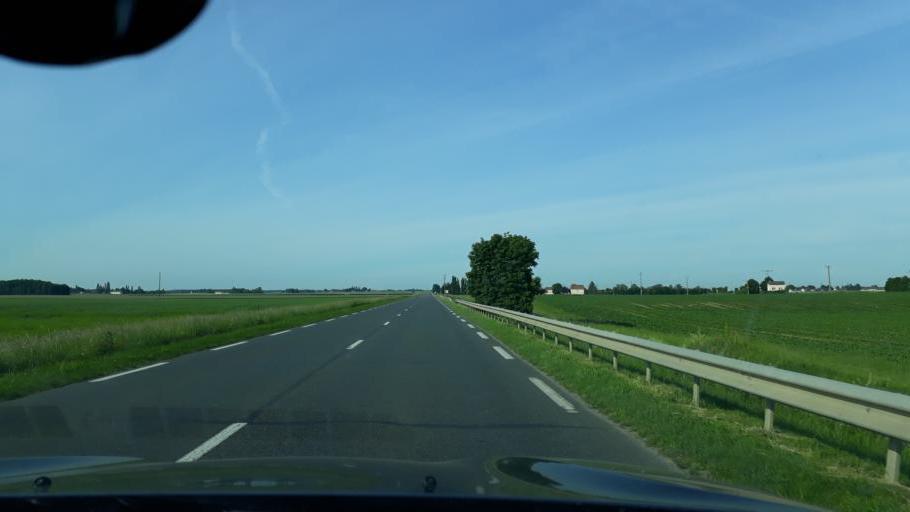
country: FR
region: Centre
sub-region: Departement du Loiret
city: Chilleurs-aux-Bois
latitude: 48.1115
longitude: 2.1774
